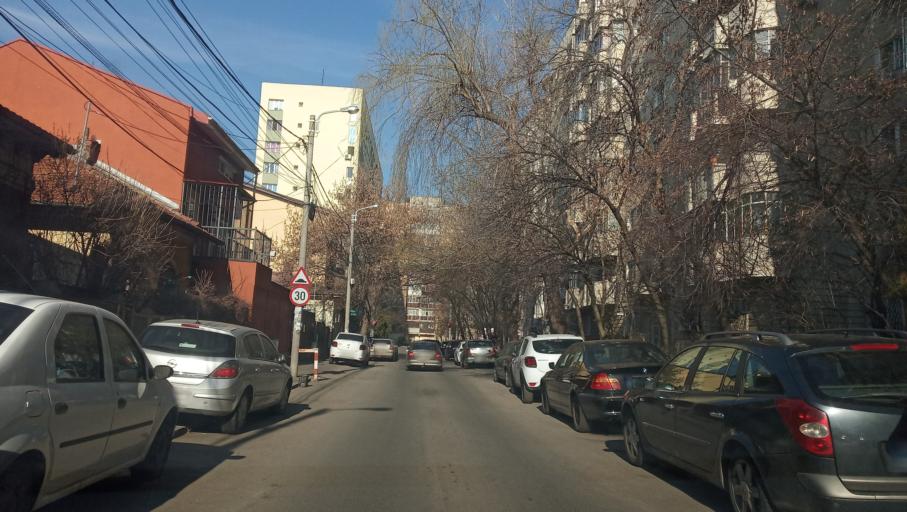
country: RO
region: Ilfov
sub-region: Comuna Fundeni-Dobroesti
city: Fundeni
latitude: 44.4609
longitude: 26.1359
